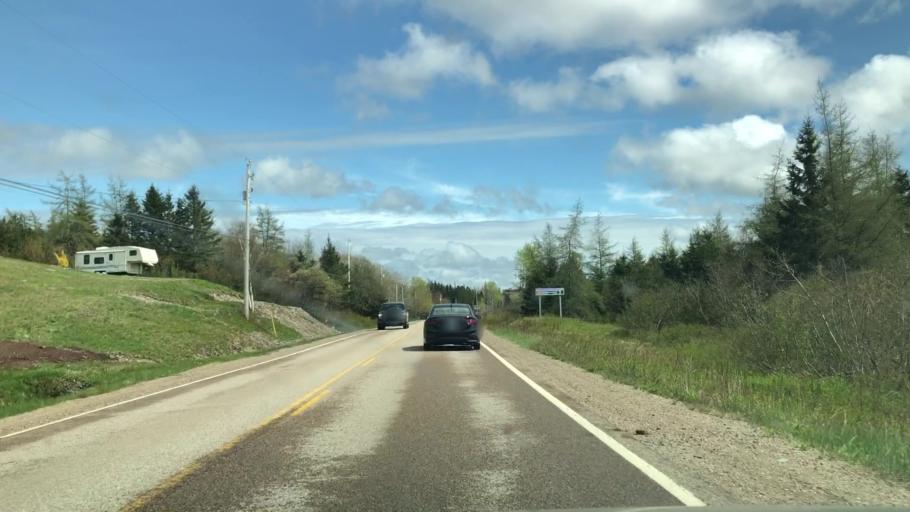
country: CA
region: Nova Scotia
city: Antigonish
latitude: 45.1874
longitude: -61.9865
